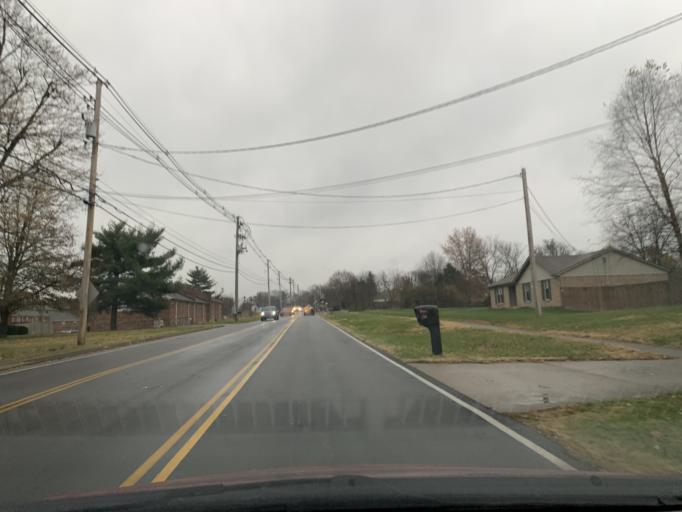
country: US
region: Kentucky
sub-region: Jefferson County
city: Saint Regis Park
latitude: 38.2003
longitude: -85.6137
